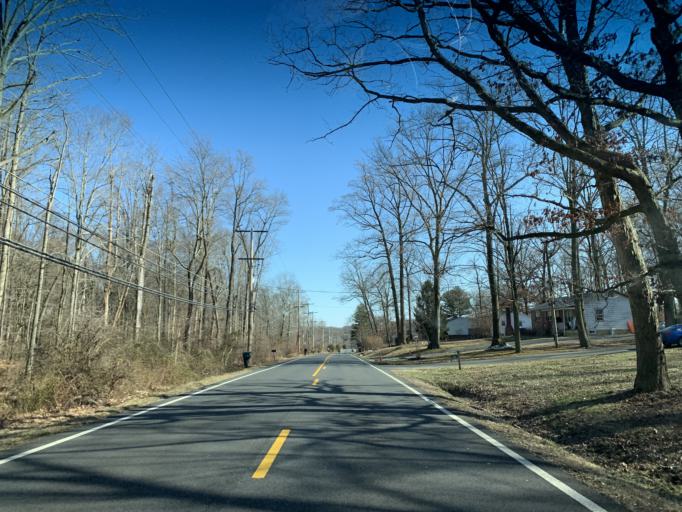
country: US
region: Maryland
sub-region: Cecil County
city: Elkton
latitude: 39.6597
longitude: -75.8892
